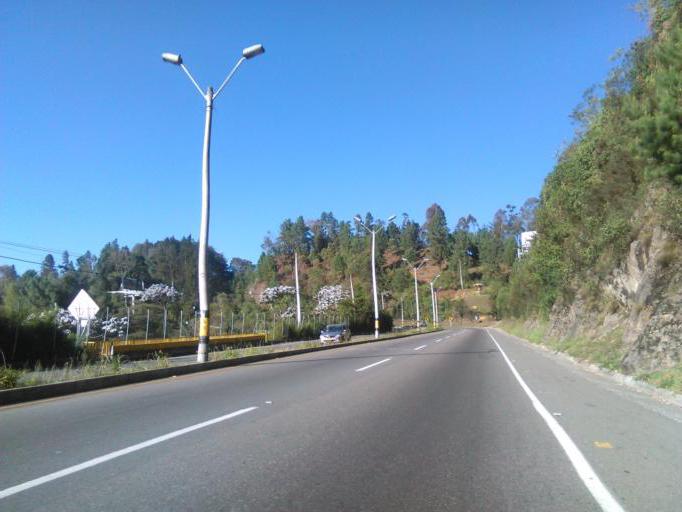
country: CO
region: Antioquia
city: Envigado
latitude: 6.1521
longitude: -75.5443
